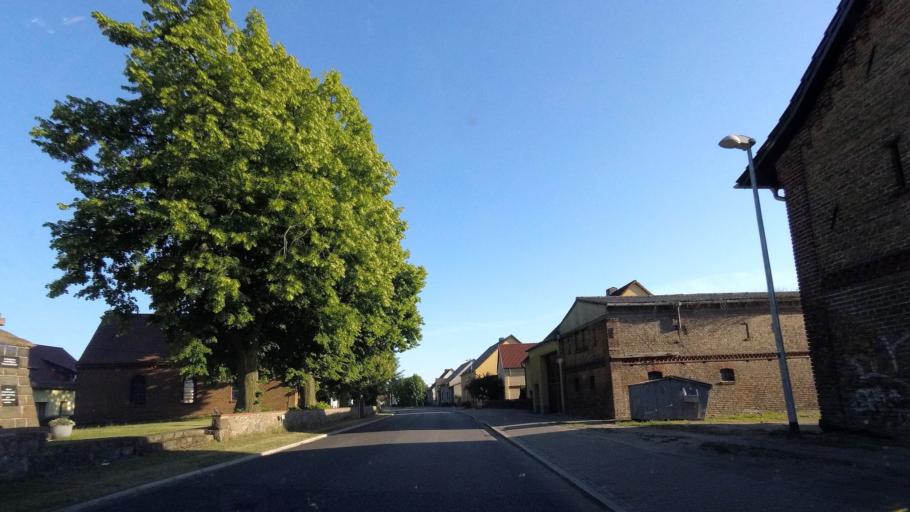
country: DE
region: Brandenburg
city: Golzow
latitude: 52.2888
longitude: 12.6014
